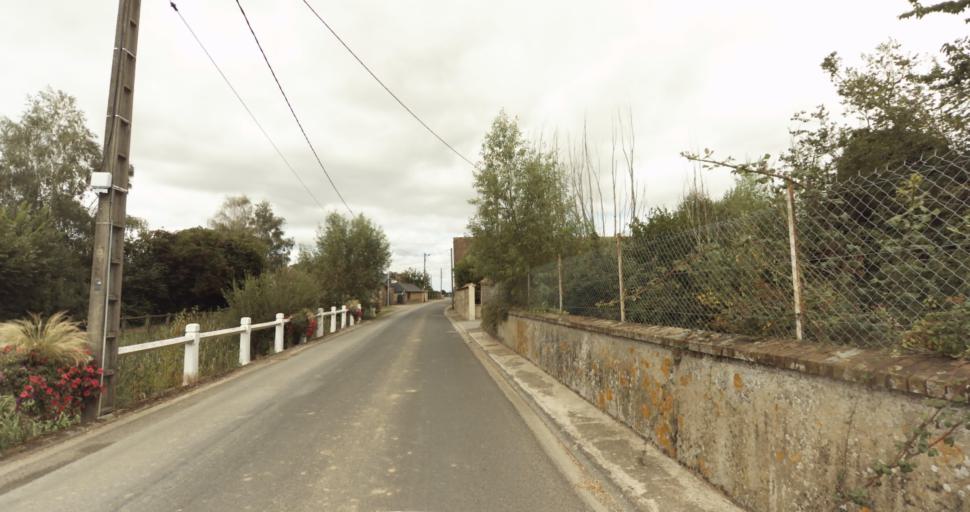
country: FR
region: Haute-Normandie
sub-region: Departement de l'Eure
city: Evreux
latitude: 48.9409
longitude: 1.1984
